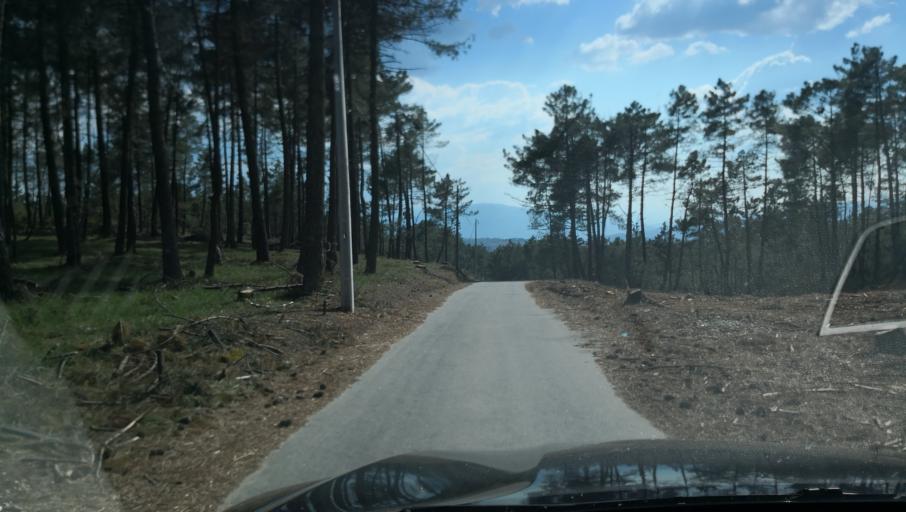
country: PT
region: Vila Real
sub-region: Sabrosa
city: Vilela
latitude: 41.2288
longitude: -7.6735
